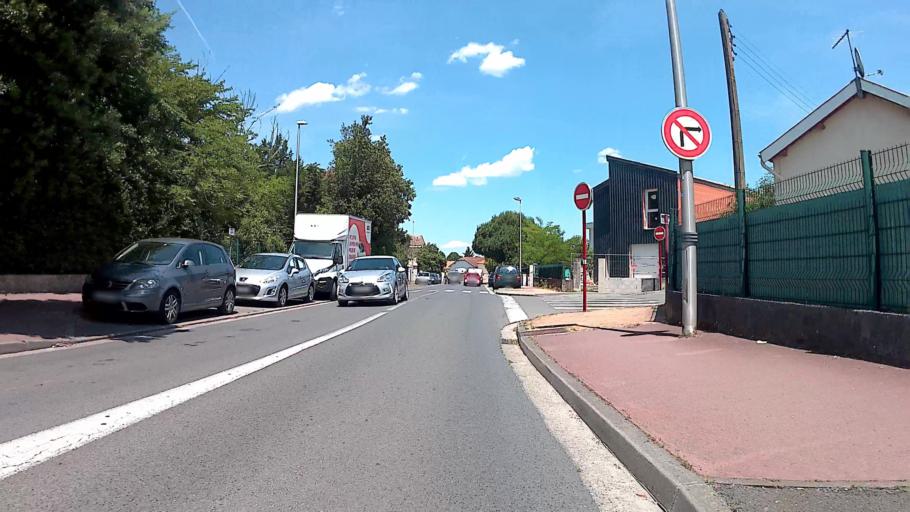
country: FR
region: Aquitaine
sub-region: Departement de la Gironde
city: Talence
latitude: 44.7999
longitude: -0.5764
